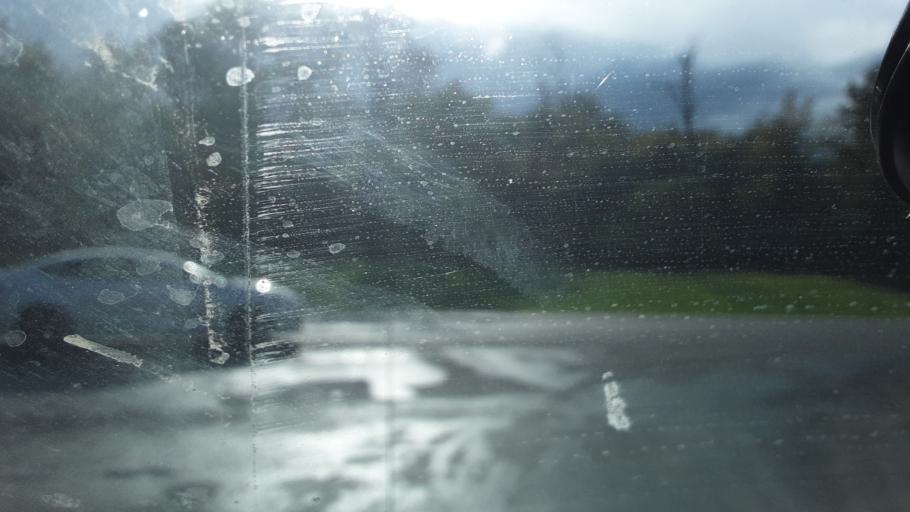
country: US
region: Ohio
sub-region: Morrow County
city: Mount Gilead
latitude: 40.5226
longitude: -82.7517
